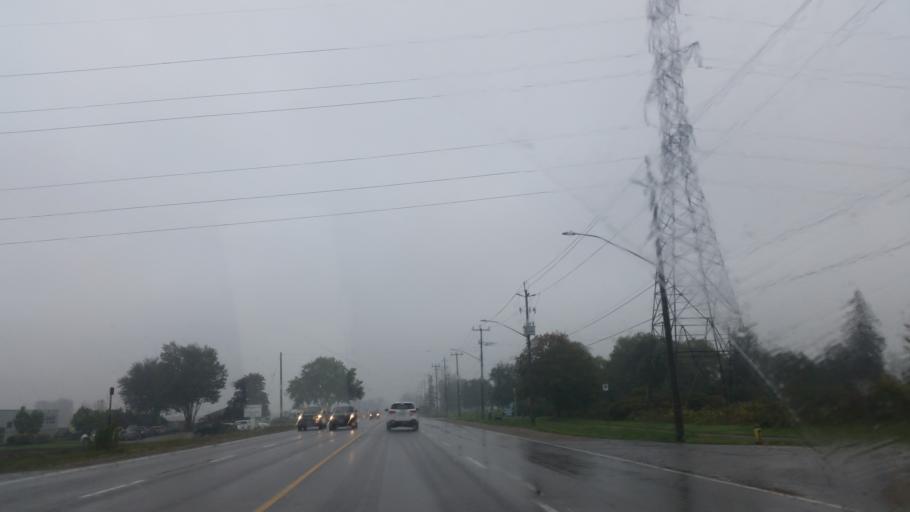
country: CA
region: Ontario
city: Stratford
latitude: 43.3461
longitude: -81.0043
